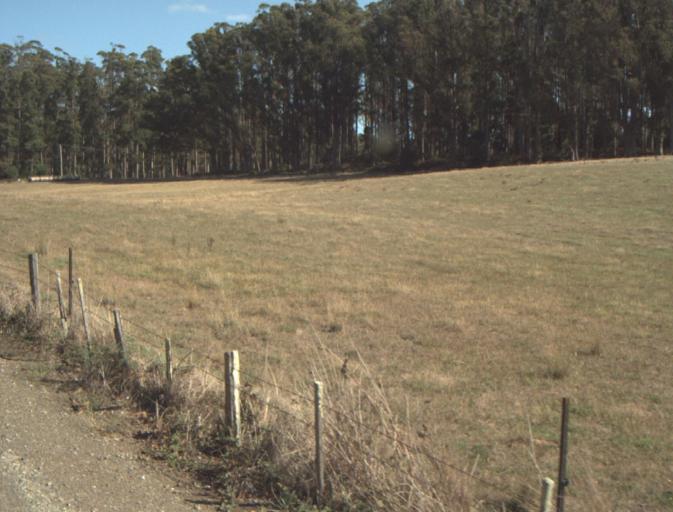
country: AU
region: Tasmania
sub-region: Launceston
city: Mayfield
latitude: -41.2286
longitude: 147.2360
